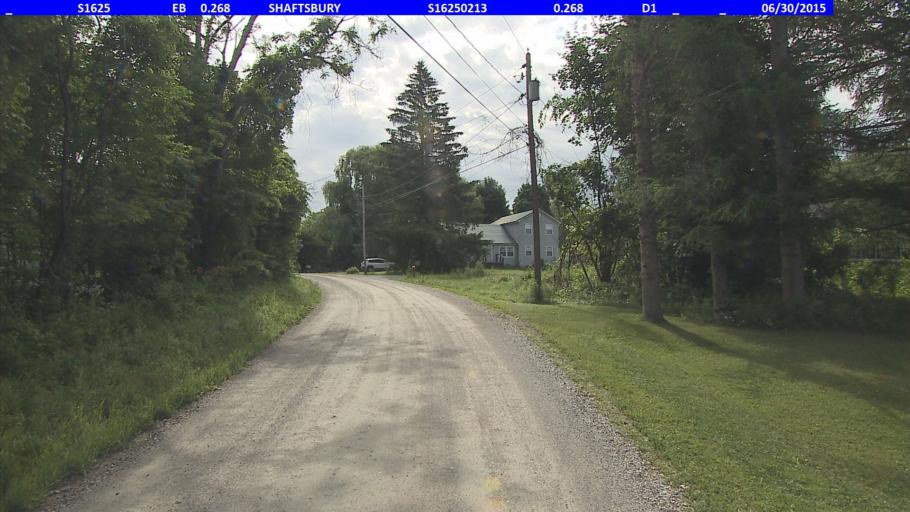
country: US
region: Vermont
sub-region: Bennington County
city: North Bennington
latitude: 42.9371
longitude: -73.2469
